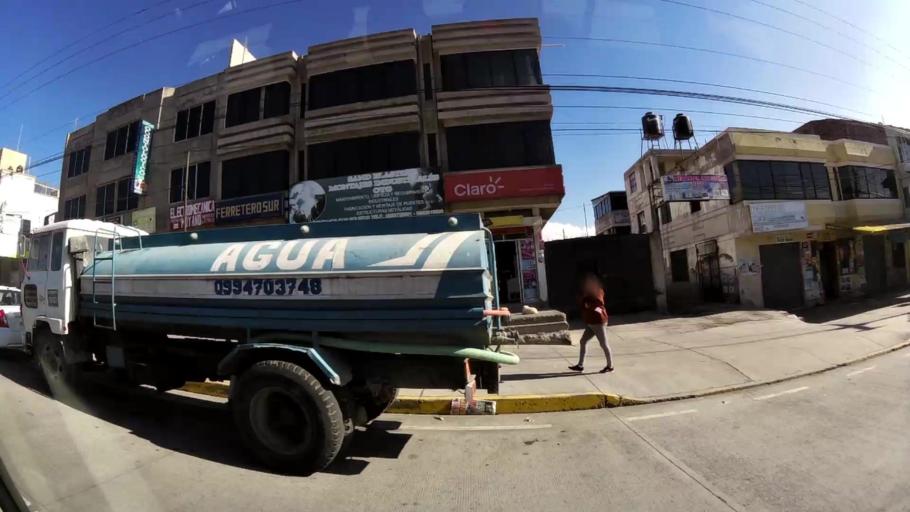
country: EC
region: Chimborazo
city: Riobamba
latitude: -1.6594
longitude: -78.6841
